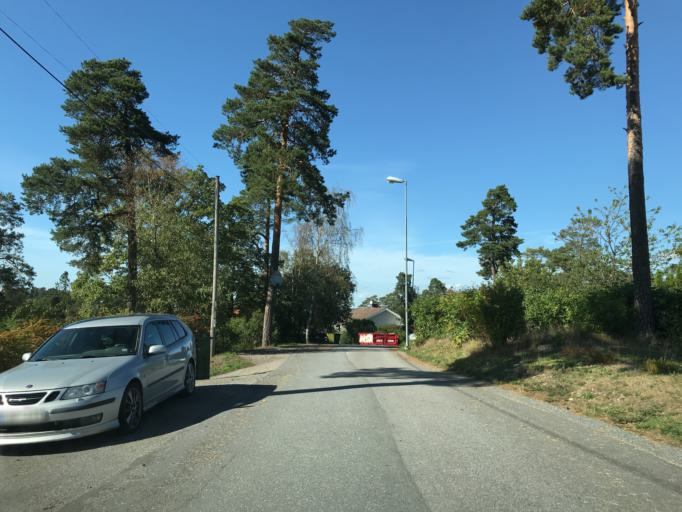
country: SE
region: Stockholm
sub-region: Sollentuna Kommun
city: Sollentuna
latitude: 59.4245
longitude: 17.9664
